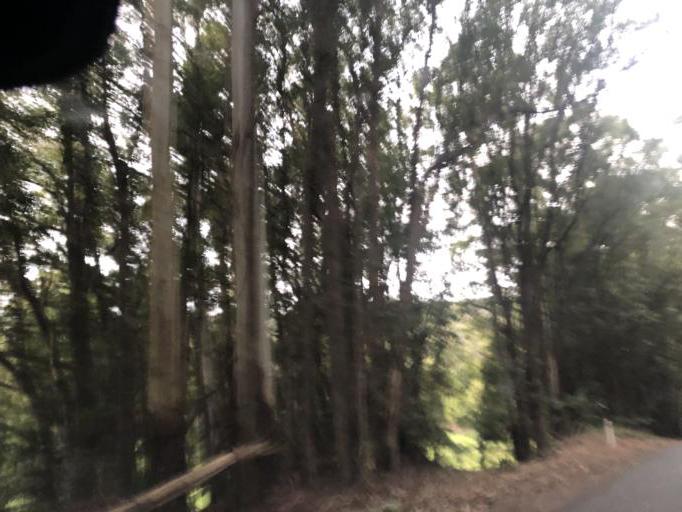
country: AU
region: New South Wales
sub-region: Coffs Harbour
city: Boambee
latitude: -30.2631
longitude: 153.0168
